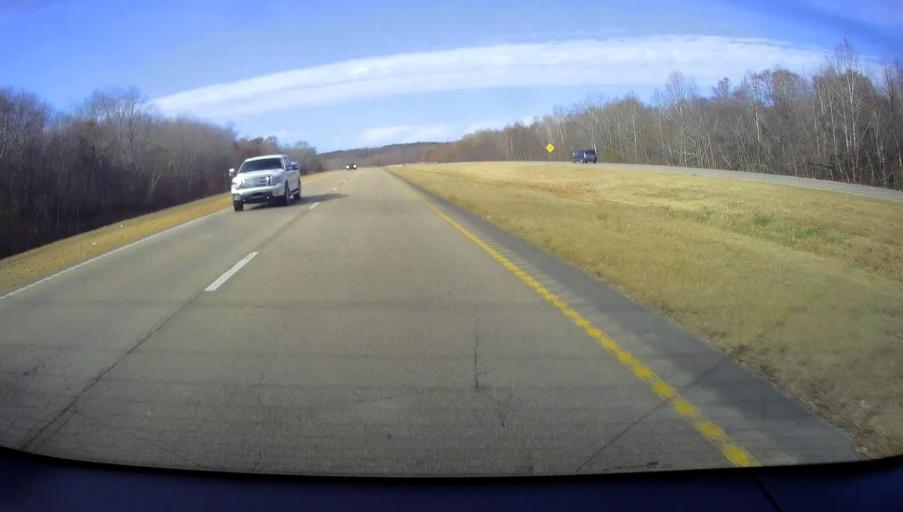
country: US
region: Mississippi
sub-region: Alcorn County
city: Corinth
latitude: 34.9415
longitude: -88.7822
